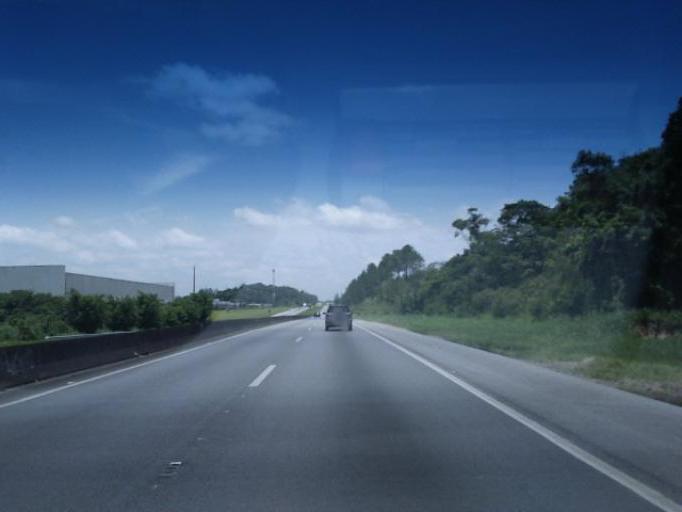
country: BR
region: Sao Paulo
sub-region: Registro
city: Registro
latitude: -24.4423
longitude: -47.7995
